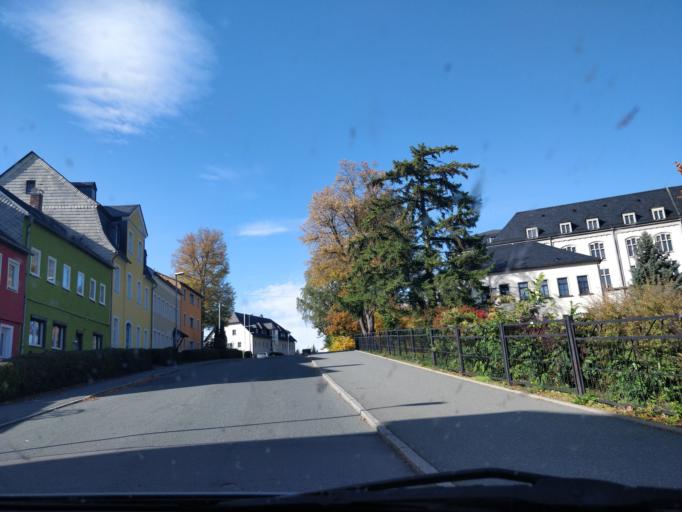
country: DE
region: Saxony
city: Schneeberg
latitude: 50.5971
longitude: 12.6387
